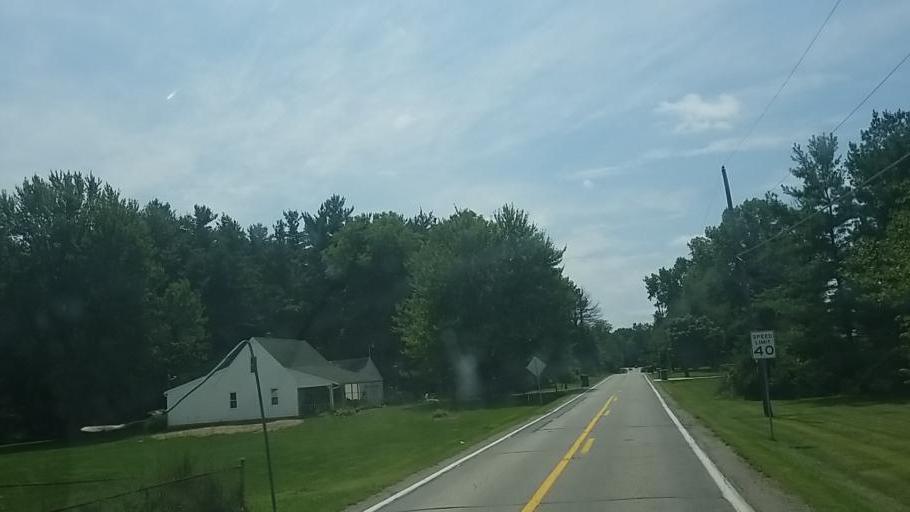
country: US
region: Ohio
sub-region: Franklin County
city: New Albany
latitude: 40.0510
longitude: -82.7772
